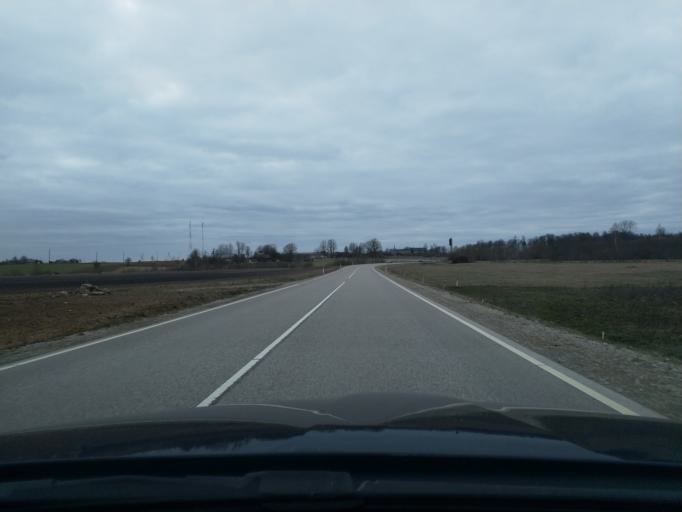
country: LV
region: Talsu Rajons
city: Sabile
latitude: 56.9438
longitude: 22.4142
